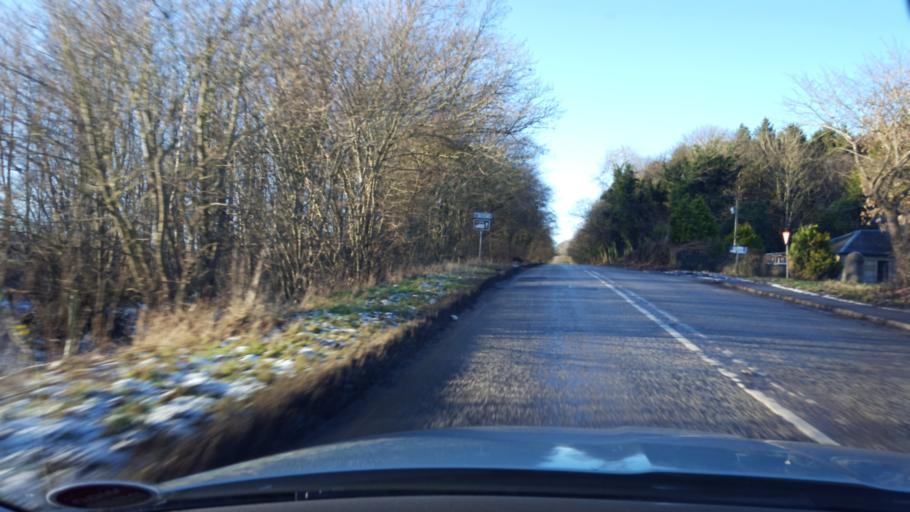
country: GB
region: Scotland
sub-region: West Lothian
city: Broxburn
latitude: 55.9636
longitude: -3.4924
